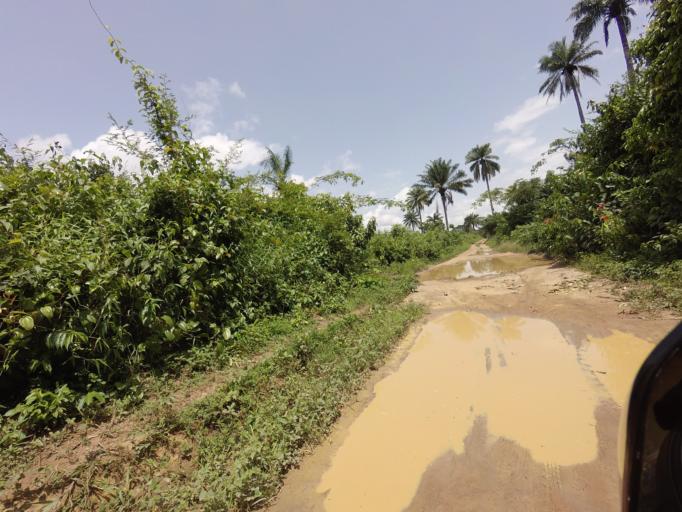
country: SL
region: Eastern Province
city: Tombodu
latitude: 8.1845
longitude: -10.5991
